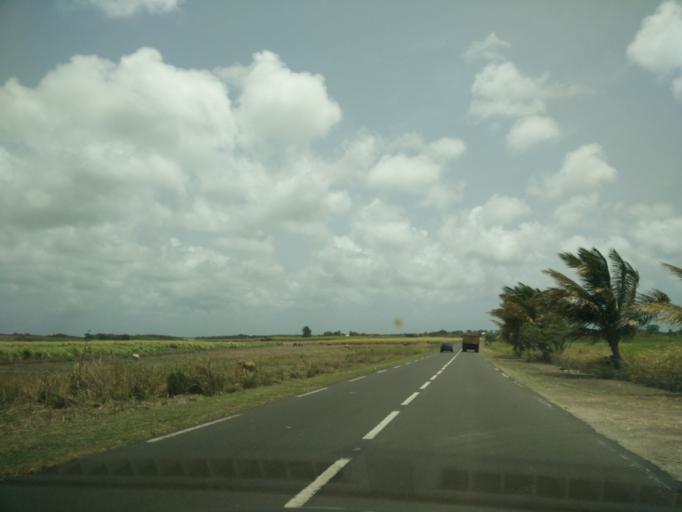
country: GP
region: Guadeloupe
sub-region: Guadeloupe
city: Petit-Canal
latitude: 16.3872
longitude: -61.4821
